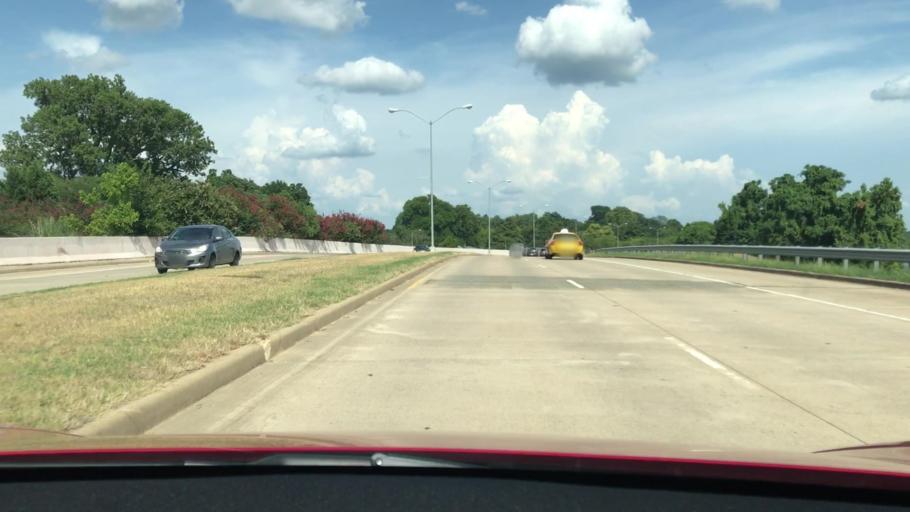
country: US
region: Louisiana
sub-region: Bossier Parish
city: Bossier City
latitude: 32.5098
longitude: -93.7188
